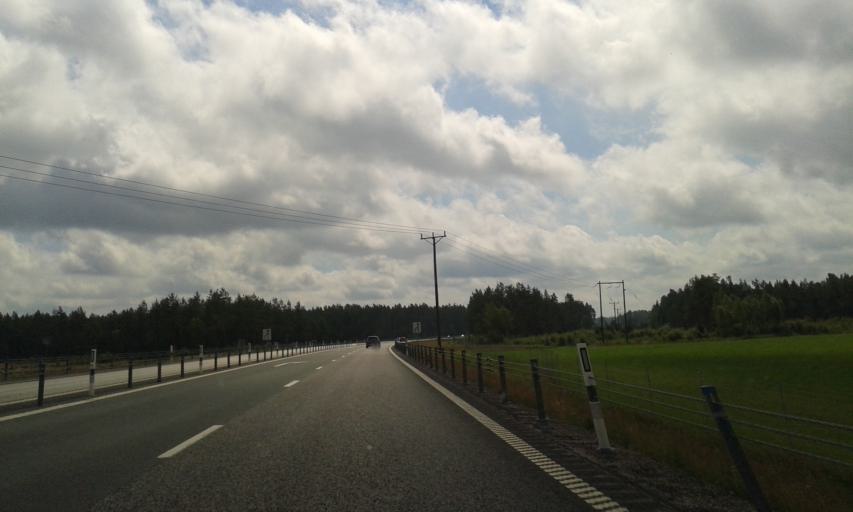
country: SE
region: Joenkoeping
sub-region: Gislaveds Kommun
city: Gislaved
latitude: 57.3144
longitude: 13.5681
